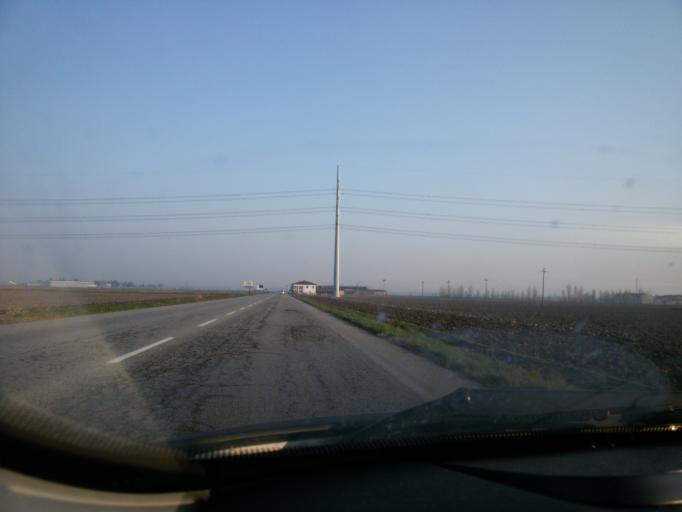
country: IT
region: Piedmont
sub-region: Provincia di Vercelli
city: Prarolo
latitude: 45.2739
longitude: 8.4636
